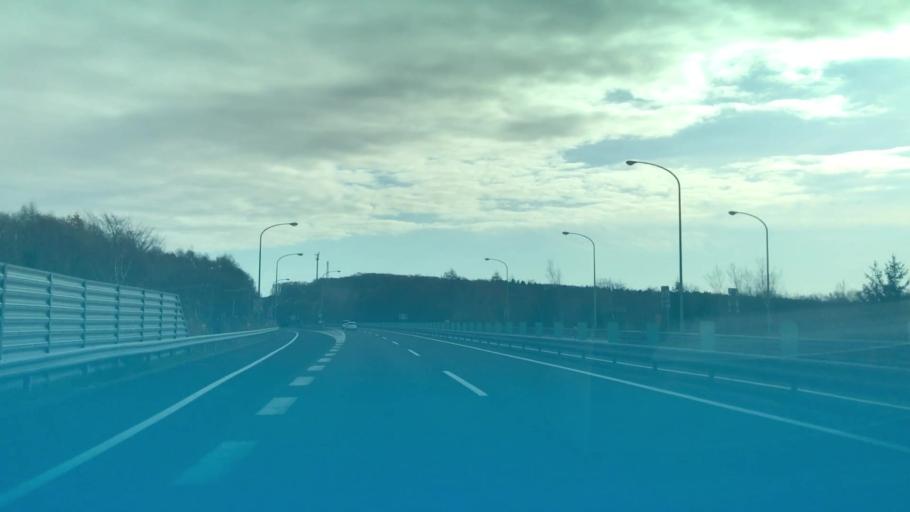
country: JP
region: Hokkaido
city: Chitose
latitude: 42.8778
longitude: 141.7296
